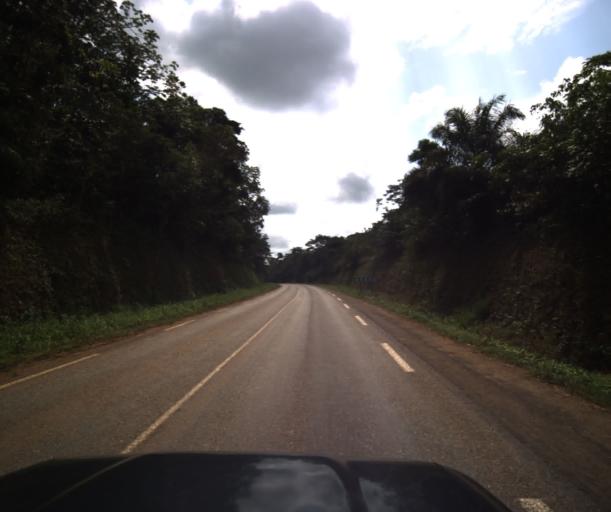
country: CM
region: Centre
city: Eseka
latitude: 3.8709
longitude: 10.6347
